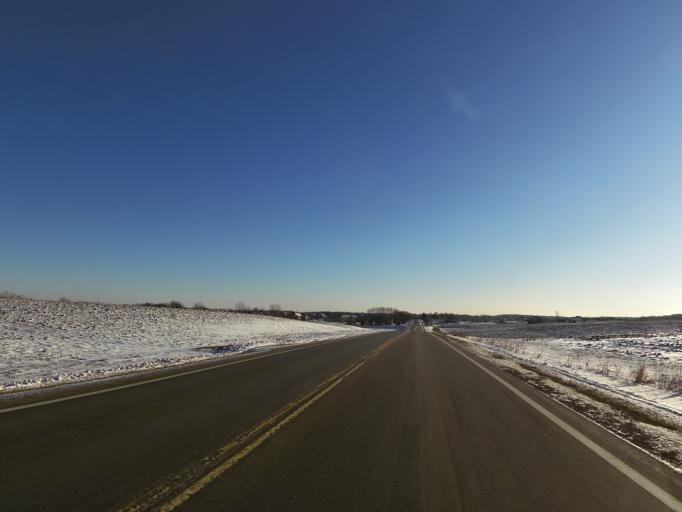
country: US
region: Minnesota
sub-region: Scott County
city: Shakopee
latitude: 44.7327
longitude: -93.5469
